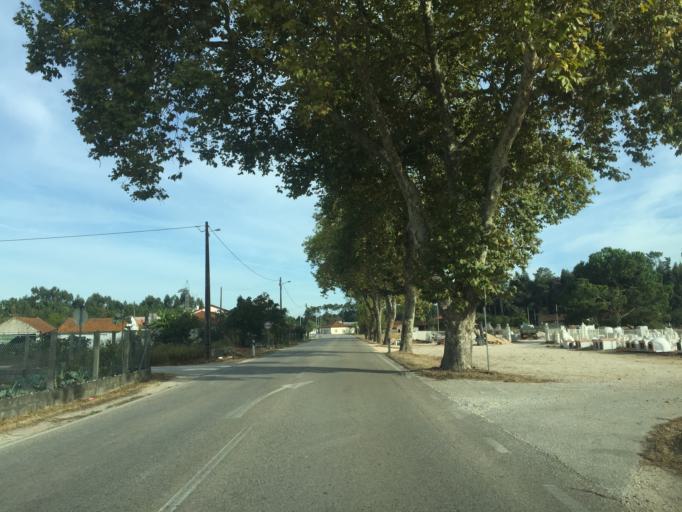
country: PT
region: Leiria
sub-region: Pombal
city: Lourical
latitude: 39.9566
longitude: -8.7865
